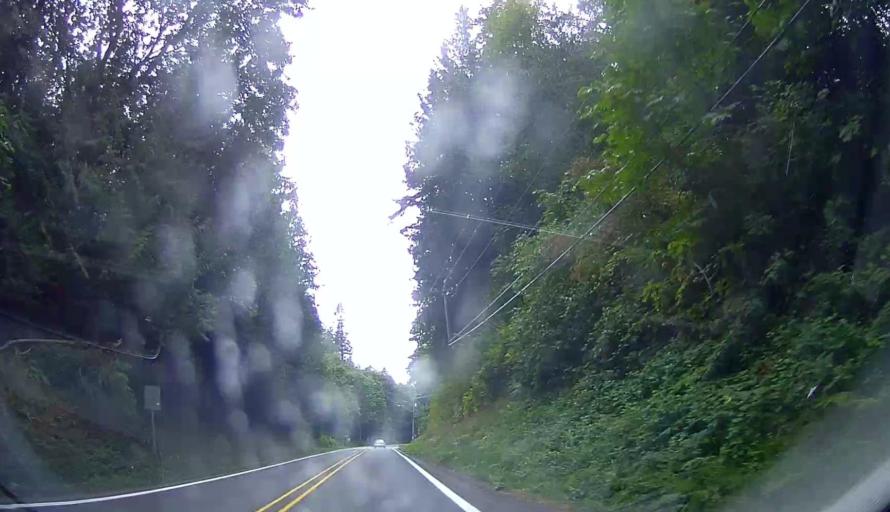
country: US
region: Washington
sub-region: Snohomish County
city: Warm Beach
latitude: 48.1226
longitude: -122.3541
